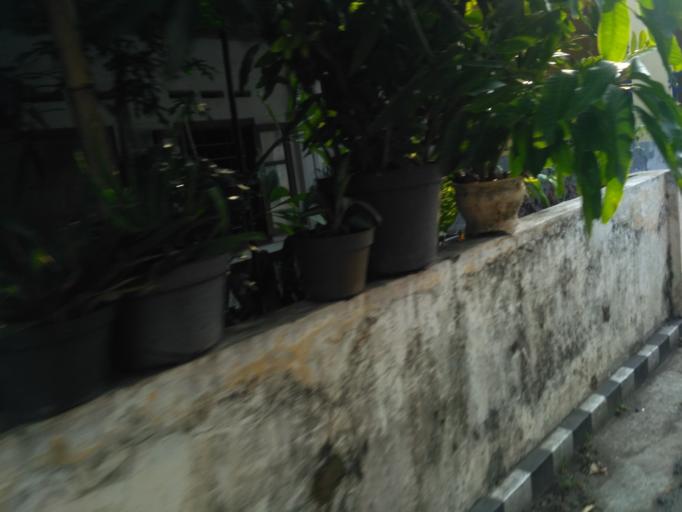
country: ID
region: East Java
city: Malang
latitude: -7.9574
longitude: 112.6258
